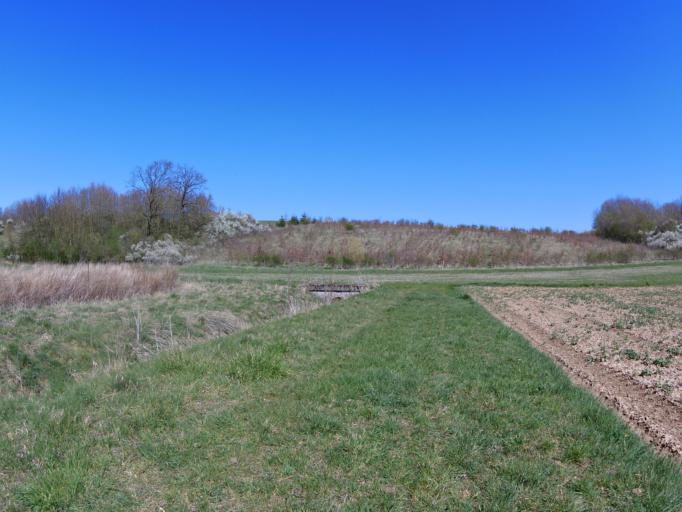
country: DE
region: Bavaria
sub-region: Regierungsbezirk Unterfranken
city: Rottendorf
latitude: 49.8176
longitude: 10.0656
